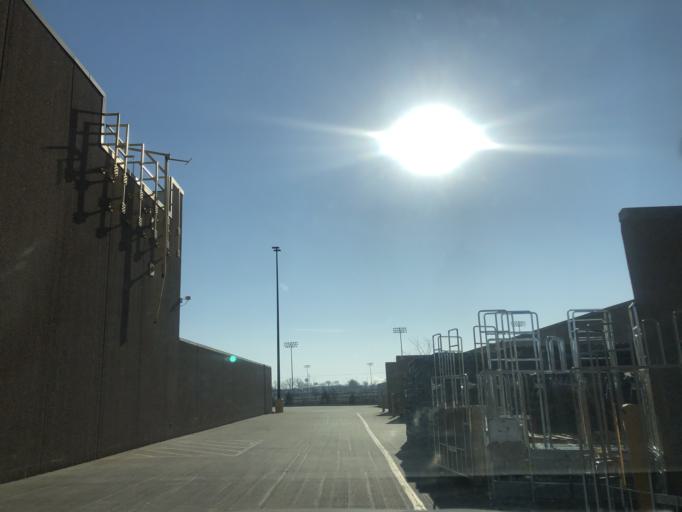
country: US
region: Illinois
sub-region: Cook County
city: Cicero
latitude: 41.8309
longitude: -87.7482
